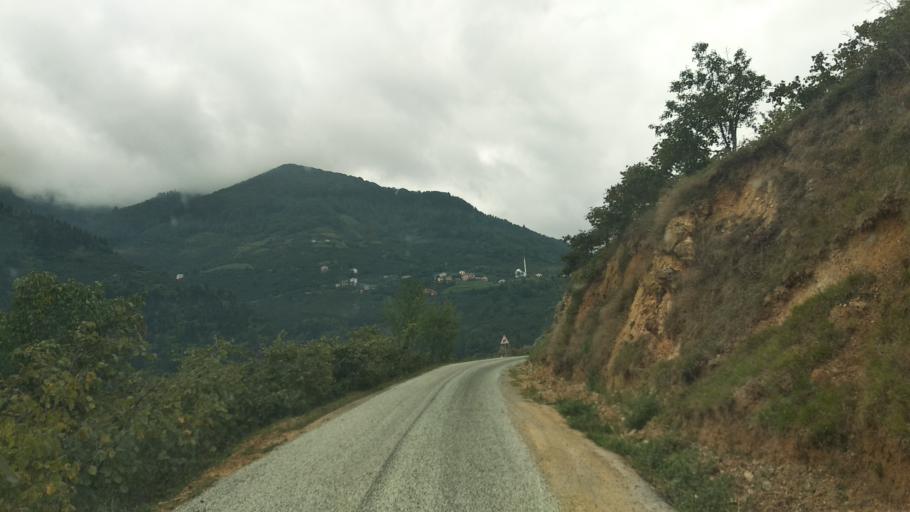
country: TR
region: Giresun
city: Dogankent
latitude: 40.7411
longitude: 38.9906
